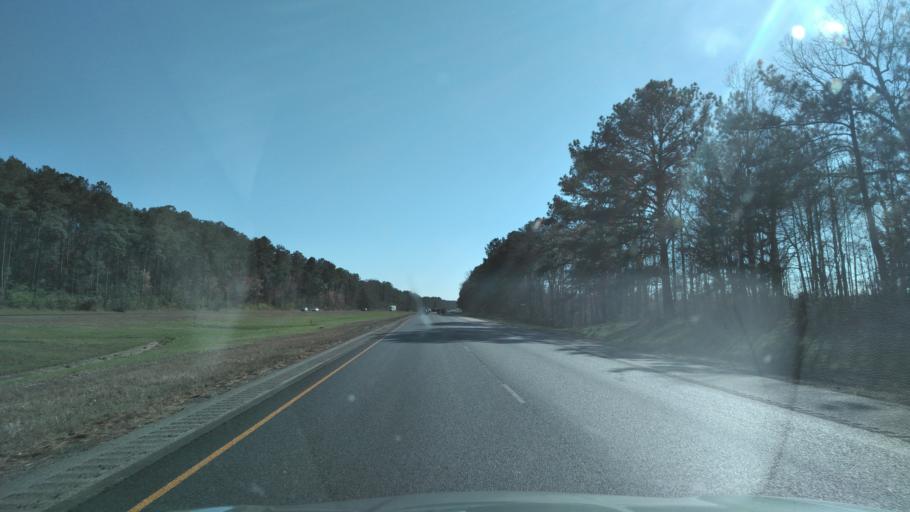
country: US
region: Alabama
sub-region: Butler County
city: Georgiana
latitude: 31.7466
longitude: -86.7105
